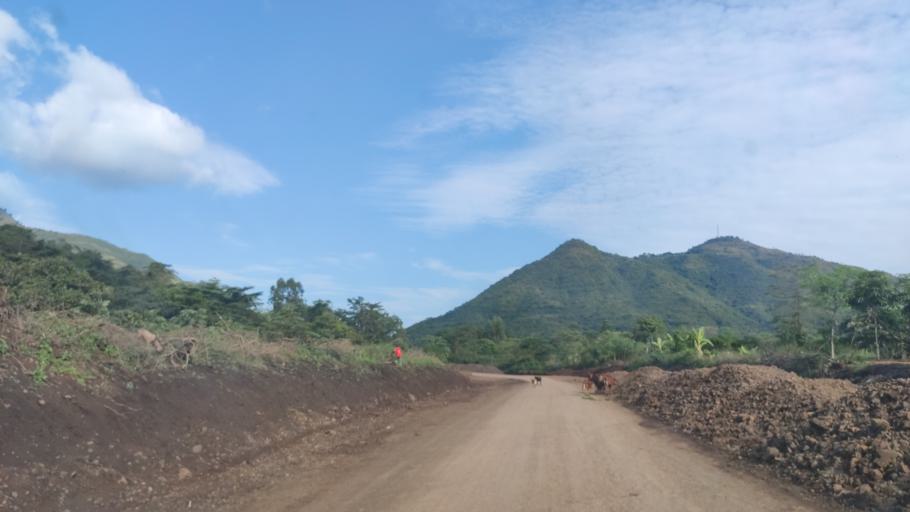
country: ET
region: Southern Nations, Nationalities, and People's Region
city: Arba Minch'
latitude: 6.4264
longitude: 37.3300
